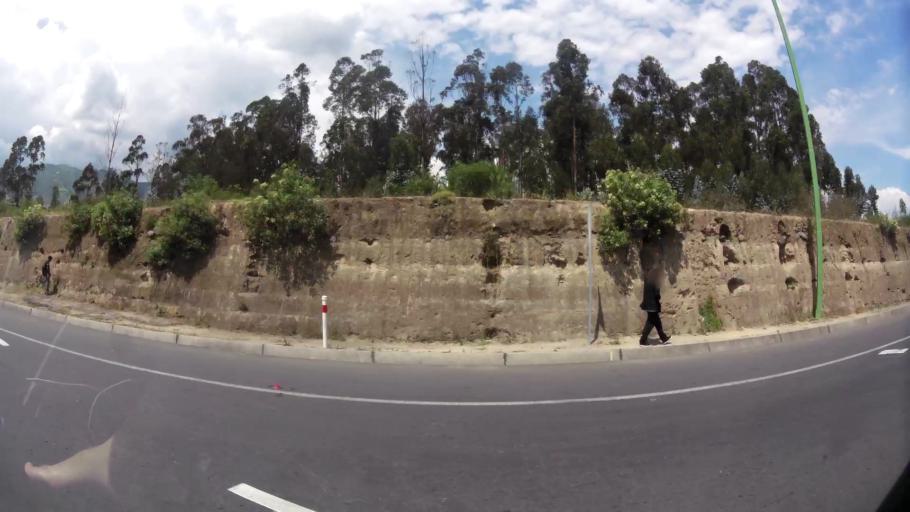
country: EC
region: Pichincha
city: Sangolqui
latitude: -0.1907
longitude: -78.3387
